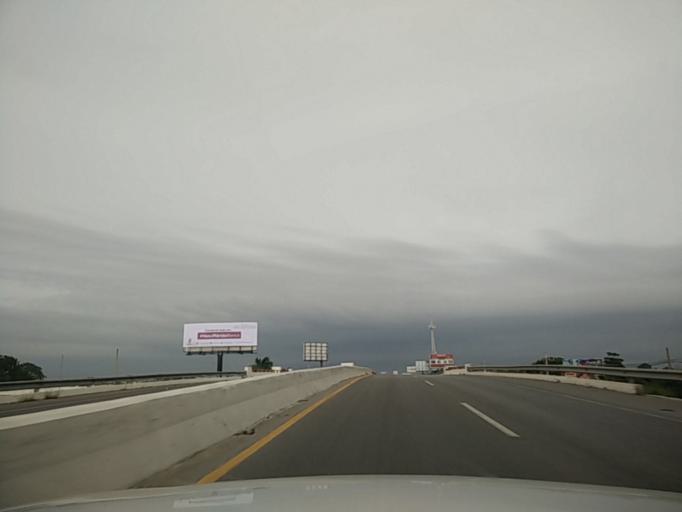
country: MX
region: Yucatan
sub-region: Kanasin
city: Kanasin
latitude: 20.9469
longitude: -89.5551
